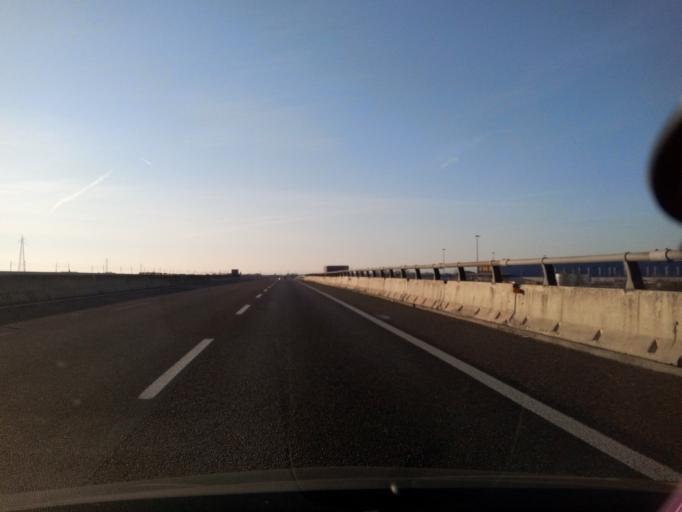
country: IT
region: Emilia-Romagna
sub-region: Provincia di Piacenza
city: Pontenure
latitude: 45.0340
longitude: 9.7653
